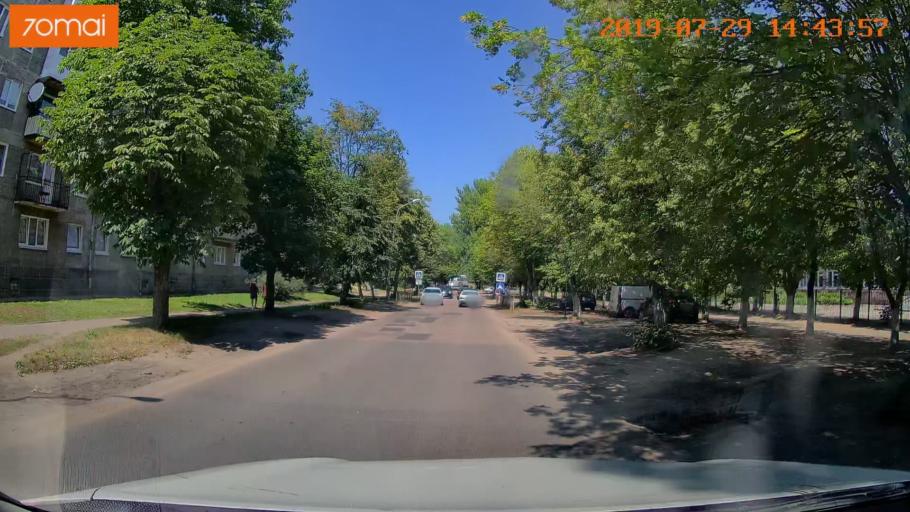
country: RU
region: Kaliningrad
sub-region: Gorod Kaliningrad
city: Baltiysk
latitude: 54.6608
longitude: 19.9078
